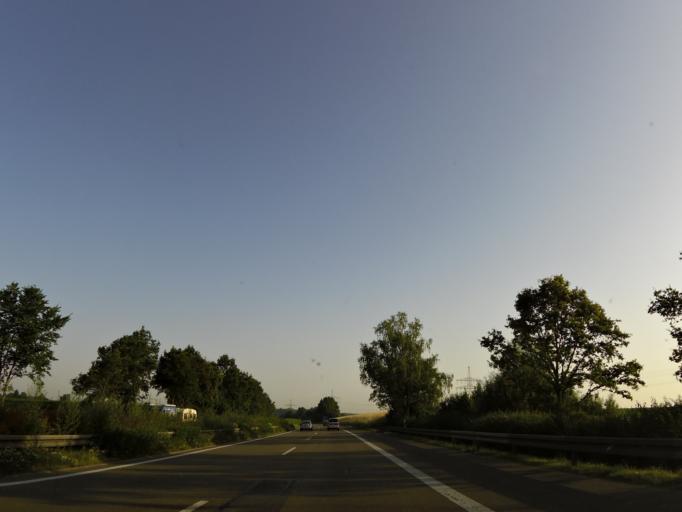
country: DE
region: Bavaria
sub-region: Swabia
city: Vohringen
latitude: 48.2915
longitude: 10.1139
